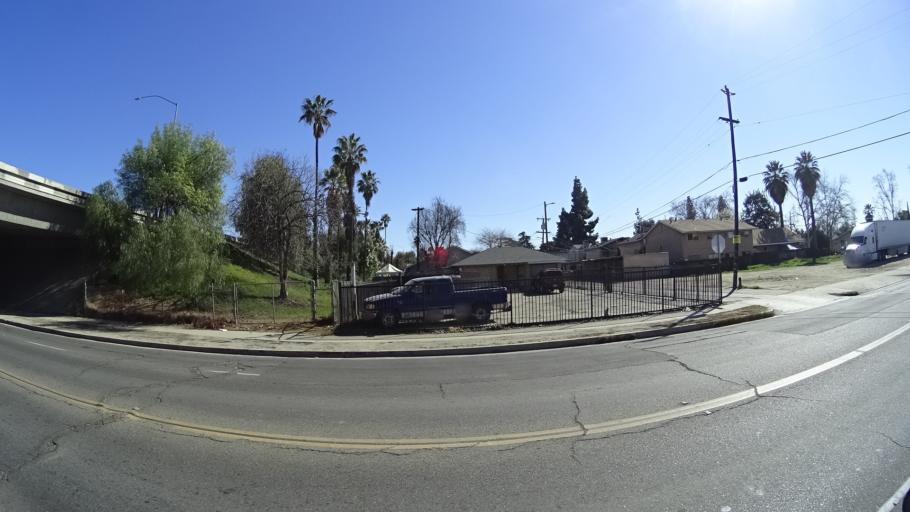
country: US
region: California
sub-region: Fresno County
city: Fresno
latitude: 36.7533
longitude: -119.7817
